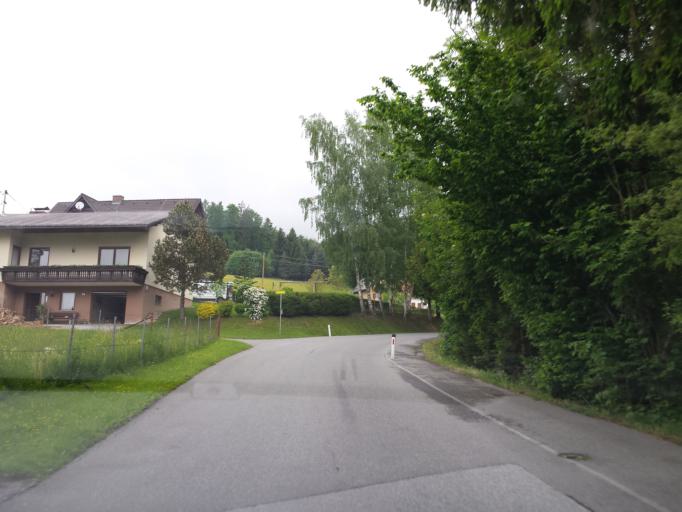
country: AT
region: Styria
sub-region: Politischer Bezirk Weiz
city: Floing
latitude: 47.2540
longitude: 15.7391
